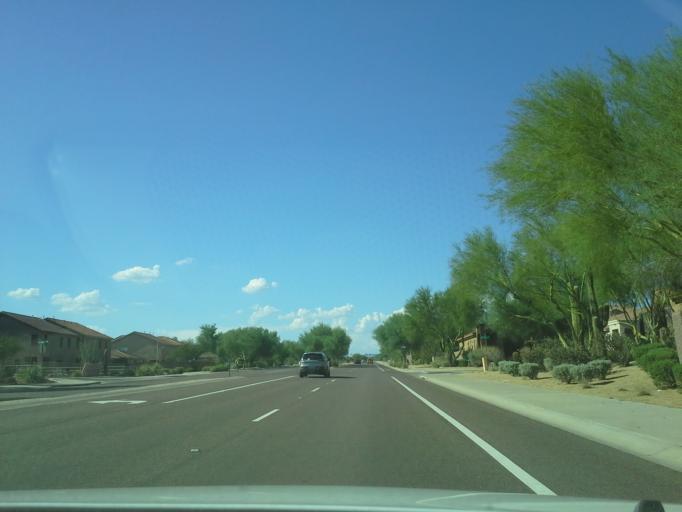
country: US
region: Arizona
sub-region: Maricopa County
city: Carefree
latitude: 33.6857
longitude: -111.9166
